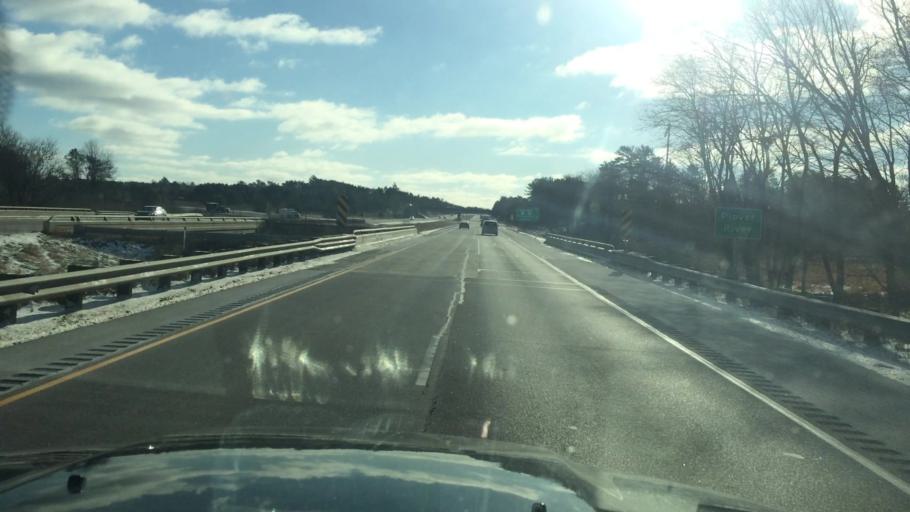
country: US
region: Wisconsin
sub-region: Portage County
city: Stevens Point
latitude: 44.5274
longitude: -89.5315
